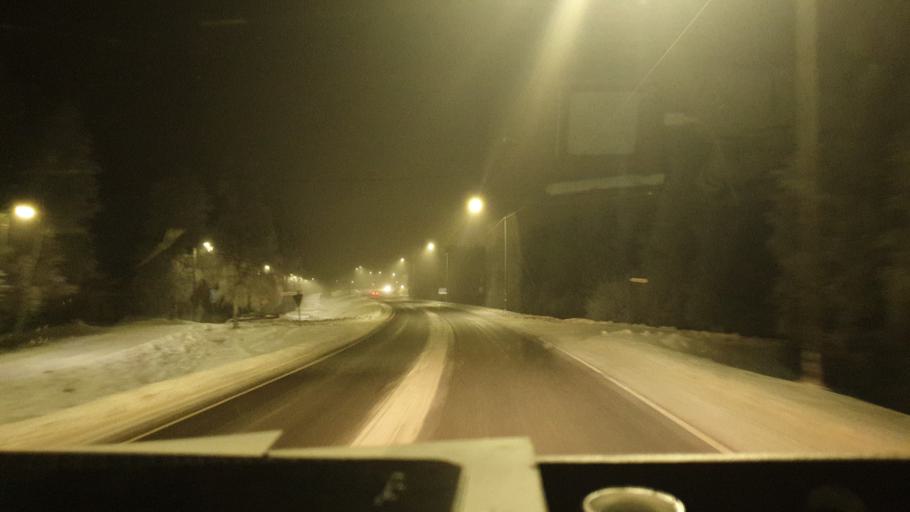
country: FI
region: Northern Ostrobothnia
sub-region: Oulunkaari
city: Ii
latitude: 65.3364
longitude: 25.3693
